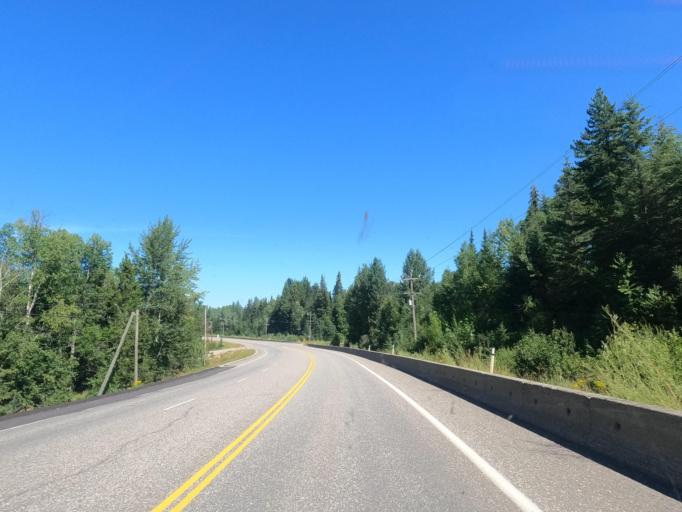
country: CA
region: British Columbia
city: Prince George
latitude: 53.5001
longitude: -122.6390
